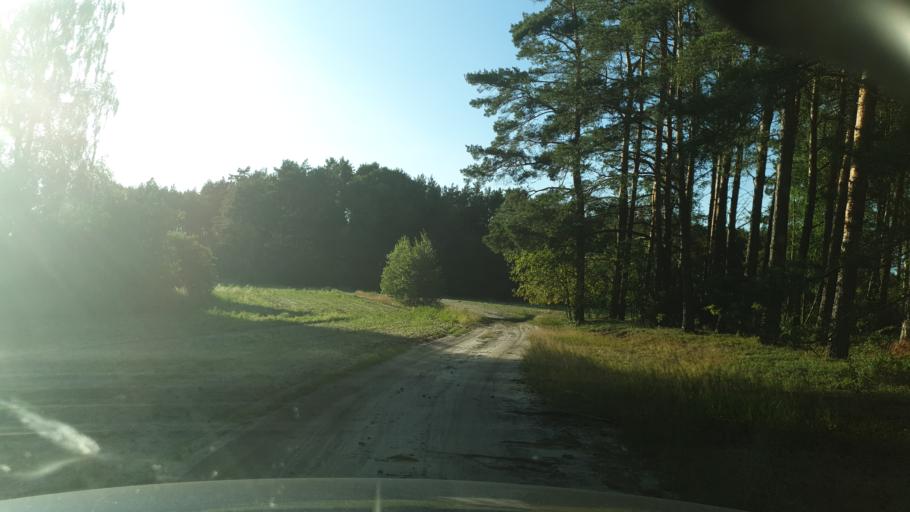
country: PL
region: Pomeranian Voivodeship
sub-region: Powiat bytowski
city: Lipnica
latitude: 53.8865
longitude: 17.4265
